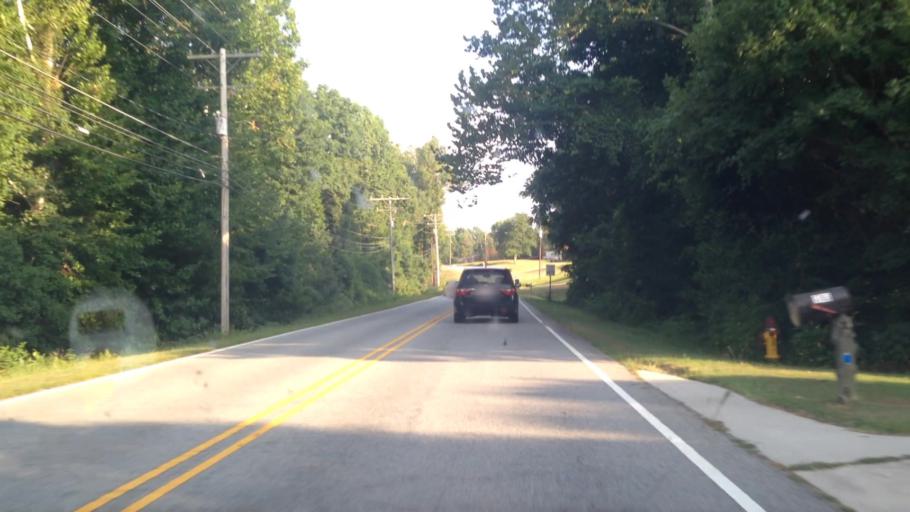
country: US
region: North Carolina
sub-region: Davidson County
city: Thomasville
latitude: 35.9447
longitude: -80.0751
